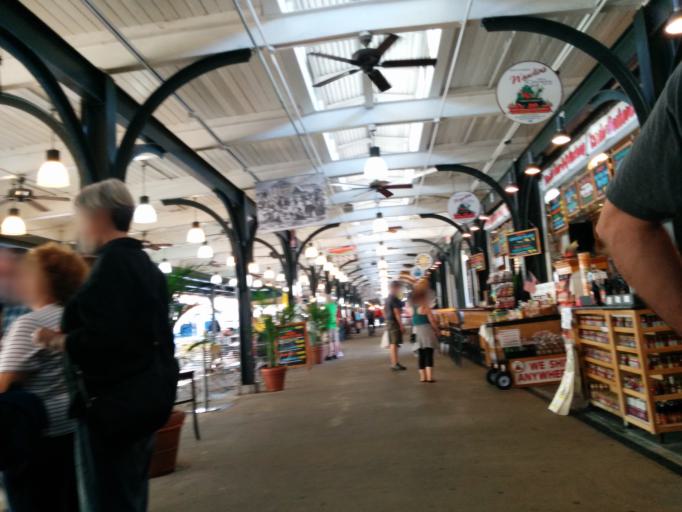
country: US
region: Louisiana
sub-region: Orleans Parish
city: New Orleans
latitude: 29.9600
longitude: -90.0593
